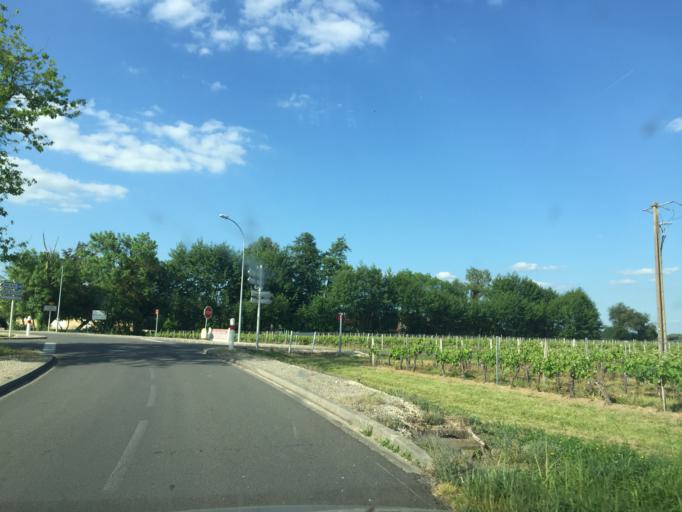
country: FR
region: Aquitaine
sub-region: Departement de la Gironde
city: Libourne
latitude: 44.9529
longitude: -0.2079
